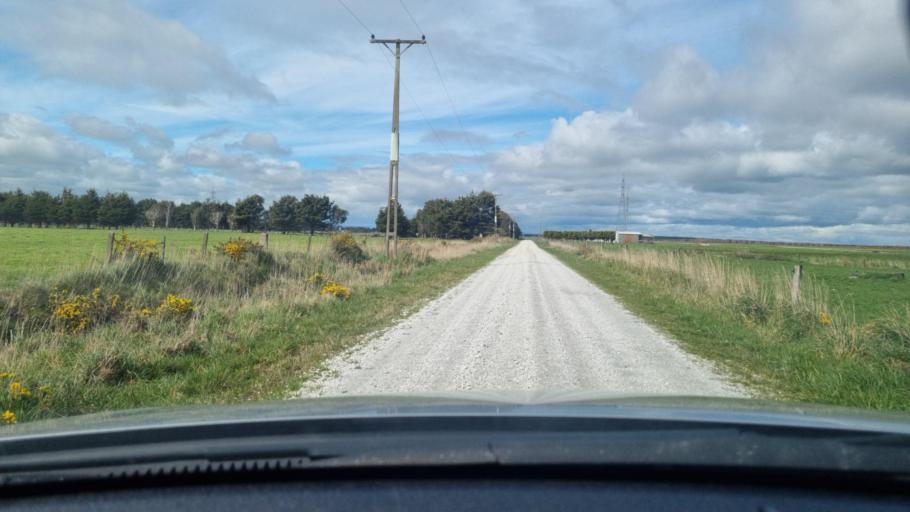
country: NZ
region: Southland
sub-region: Invercargill City
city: Invercargill
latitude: -46.4768
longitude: 168.4296
